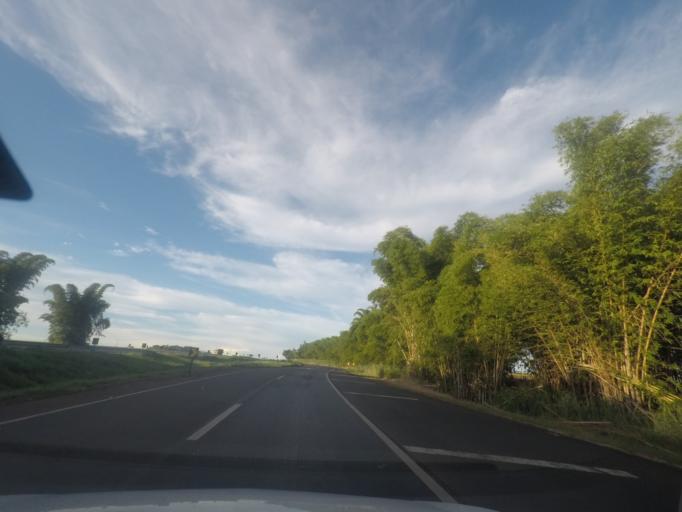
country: BR
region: Goias
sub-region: Goiatuba
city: Goiatuba
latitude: -18.1125
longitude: -49.2782
